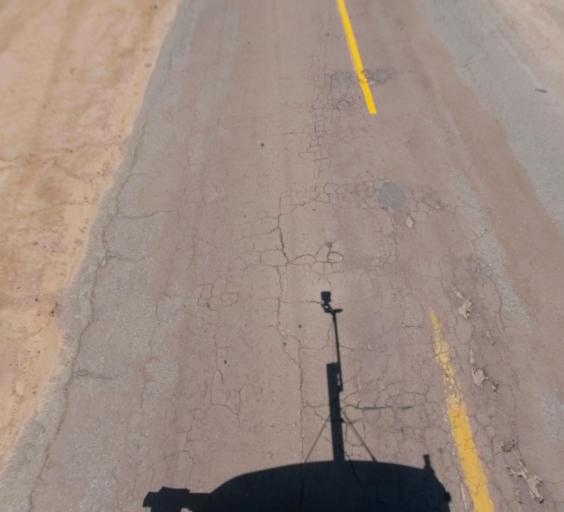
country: US
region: California
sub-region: Madera County
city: Bonadelle Ranchos-Madera Ranchos
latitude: 36.8945
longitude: -119.8230
